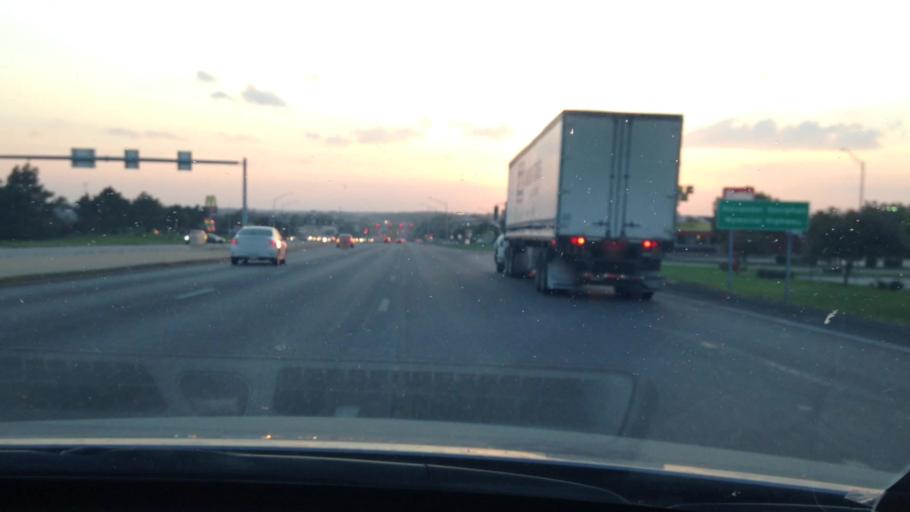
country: US
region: Missouri
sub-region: Clay County
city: Pleasant Valley
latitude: 39.2448
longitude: -94.4582
